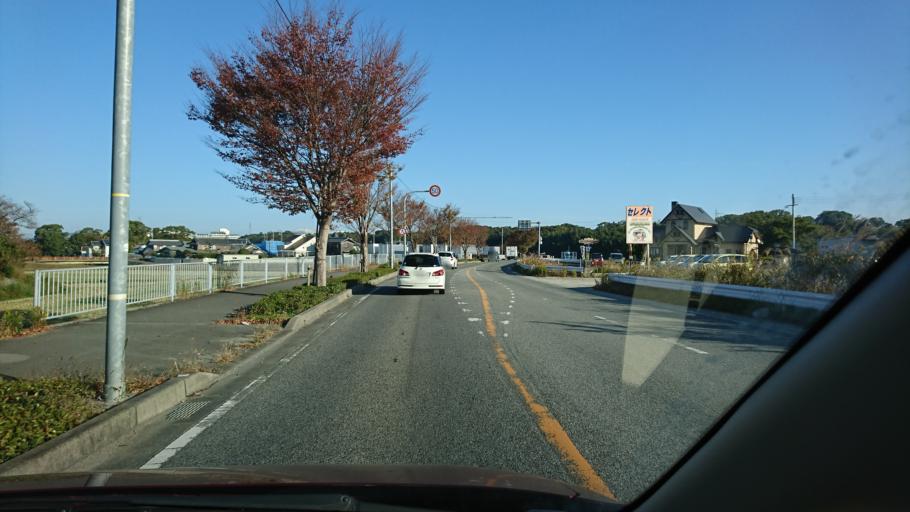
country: JP
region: Hyogo
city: Kakogawacho-honmachi
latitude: 34.7630
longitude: 134.8853
